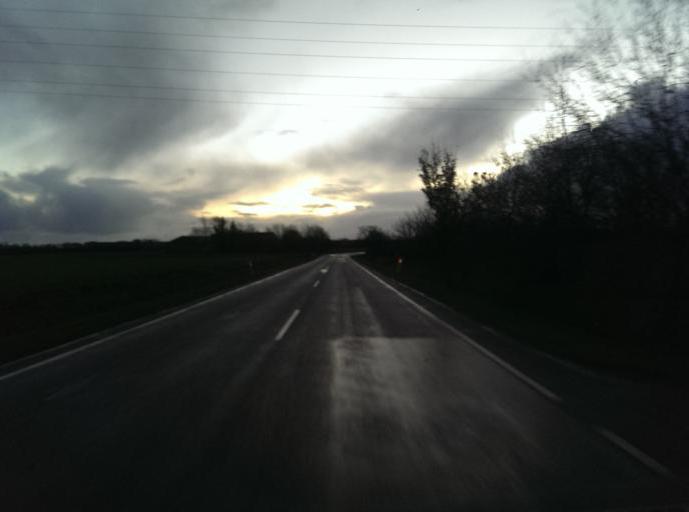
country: DK
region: South Denmark
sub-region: Esbjerg Kommune
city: Bramming
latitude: 55.4325
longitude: 8.6761
